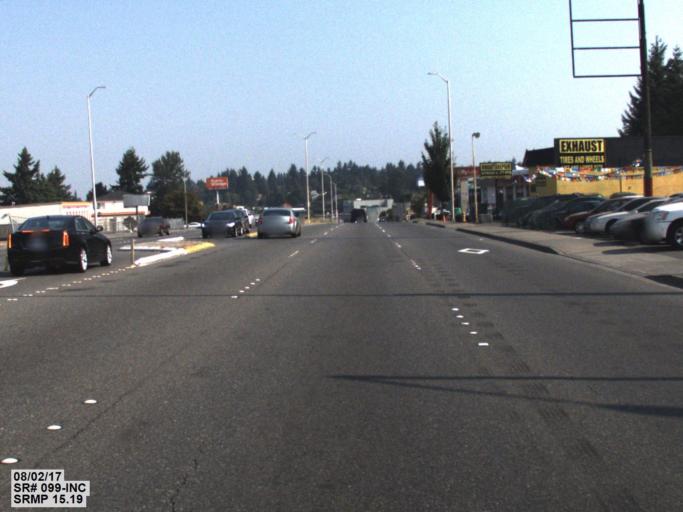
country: US
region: Washington
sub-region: King County
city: Des Moines
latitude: 47.3893
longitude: -122.2957
